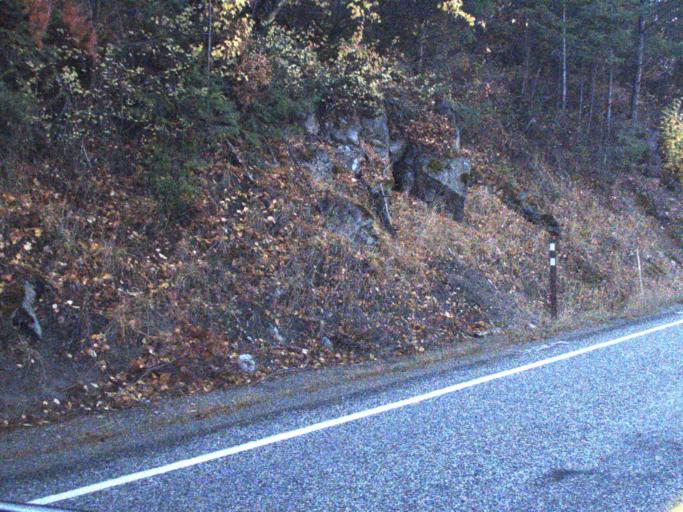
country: US
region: Washington
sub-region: Stevens County
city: Kettle Falls
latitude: 48.8136
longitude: -117.9596
